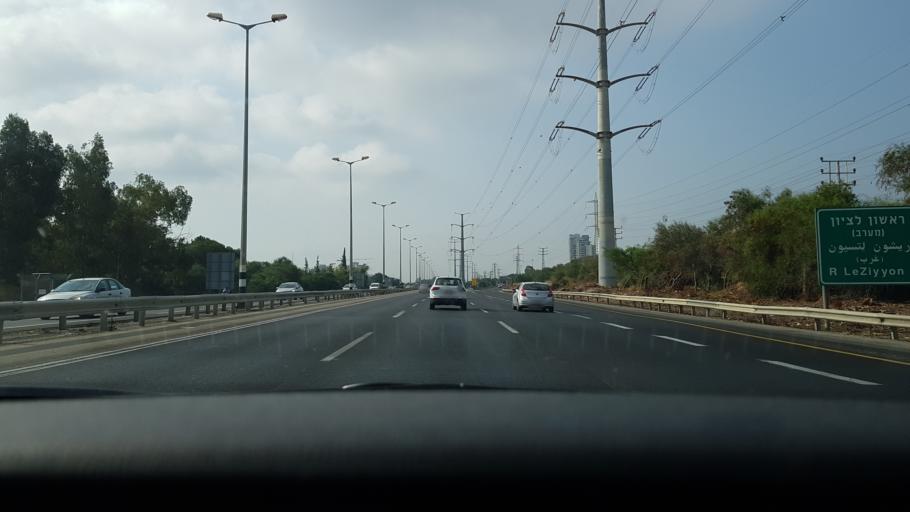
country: IL
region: Central District
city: Rishon LeZiyyon
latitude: 31.9839
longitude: 34.7951
